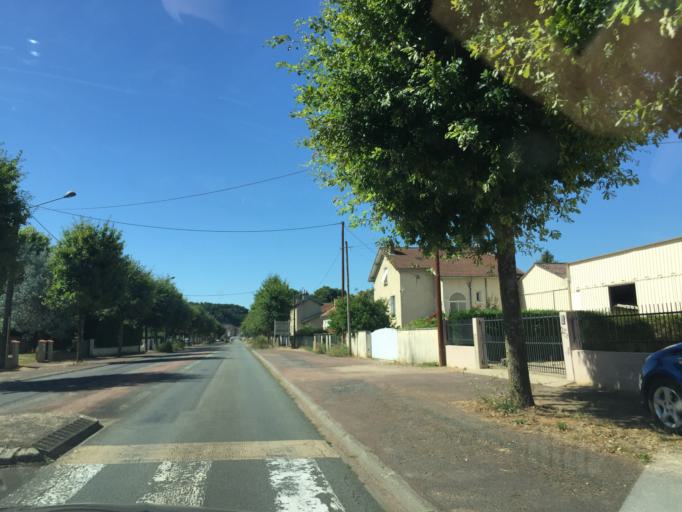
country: FR
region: Poitou-Charentes
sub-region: Departement de la Vienne
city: Lusignan
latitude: 46.4416
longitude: 0.1326
